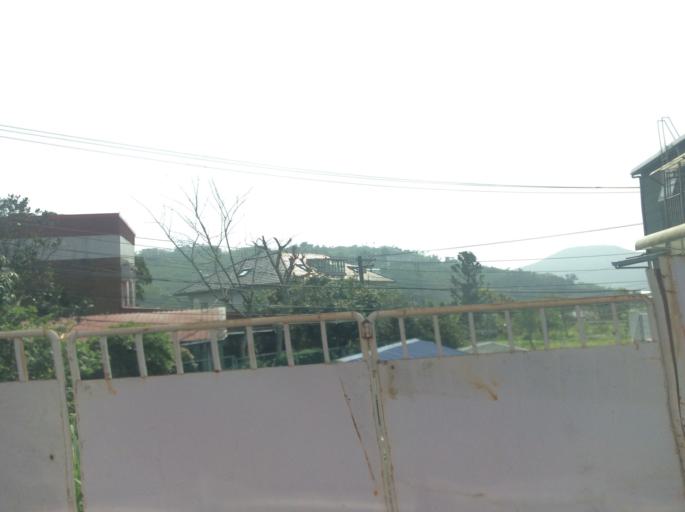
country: TW
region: Taipei
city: Taipei
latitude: 25.1191
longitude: 121.5530
